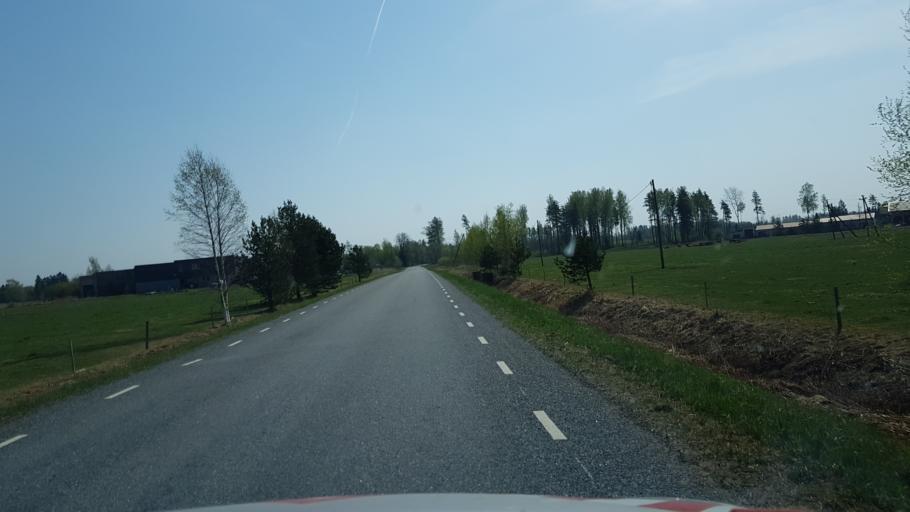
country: EE
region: Paernumaa
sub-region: Sindi linn
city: Sindi
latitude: 58.4308
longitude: 24.6396
